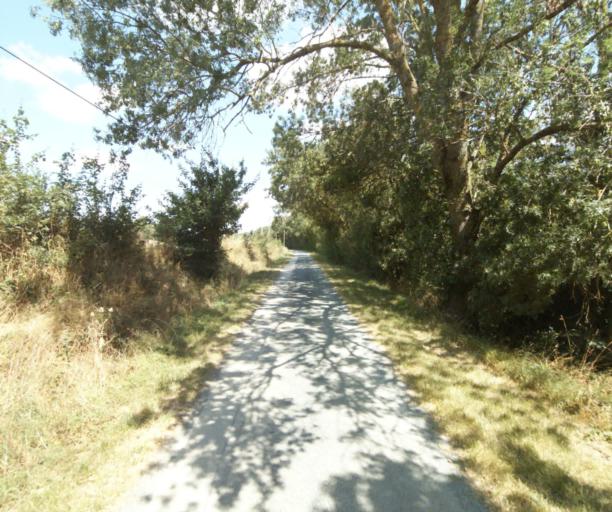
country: FR
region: Midi-Pyrenees
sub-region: Departement de la Haute-Garonne
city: Auriac-sur-Vendinelle
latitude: 43.4802
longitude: 1.8455
